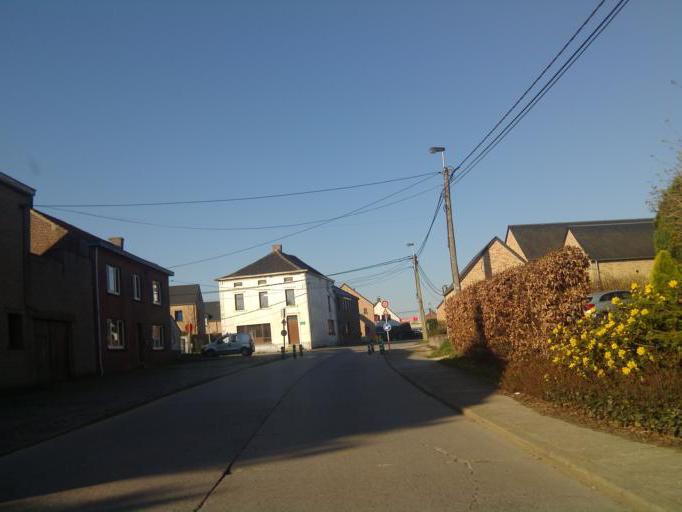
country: BE
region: Wallonia
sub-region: Province du Brabant Wallon
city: Chastre-Villeroux-Blanmont
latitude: 50.6460
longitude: 4.6496
